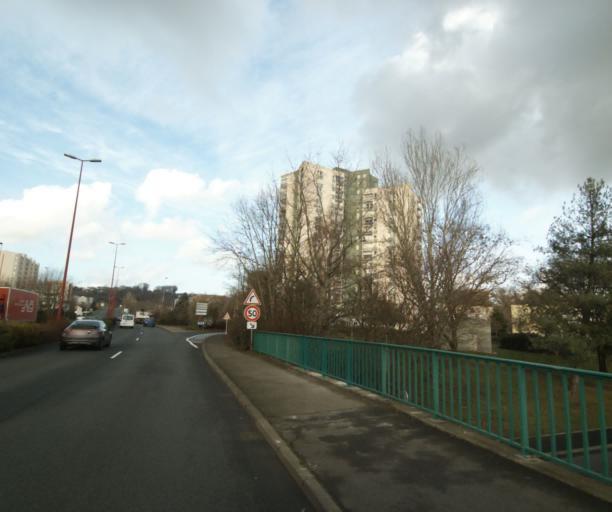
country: FR
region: Pays de la Loire
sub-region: Departement de la Sarthe
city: Le Mans
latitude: 47.9906
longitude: 0.2267
